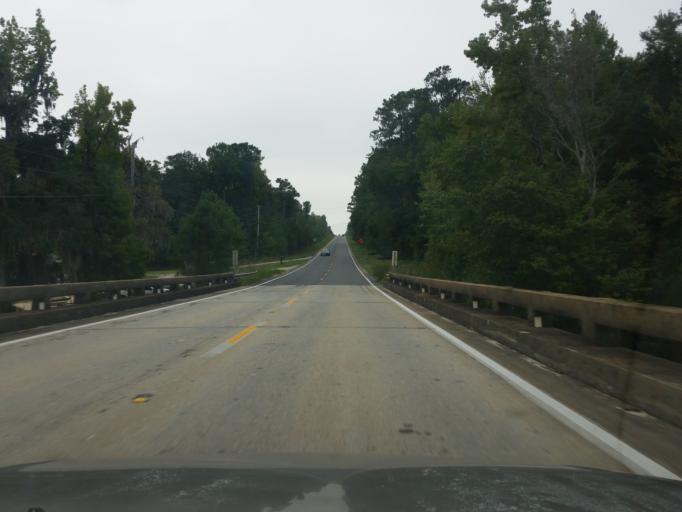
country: US
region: Alabama
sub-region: Baldwin County
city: Spanish Fort
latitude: 30.6997
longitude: -87.9023
